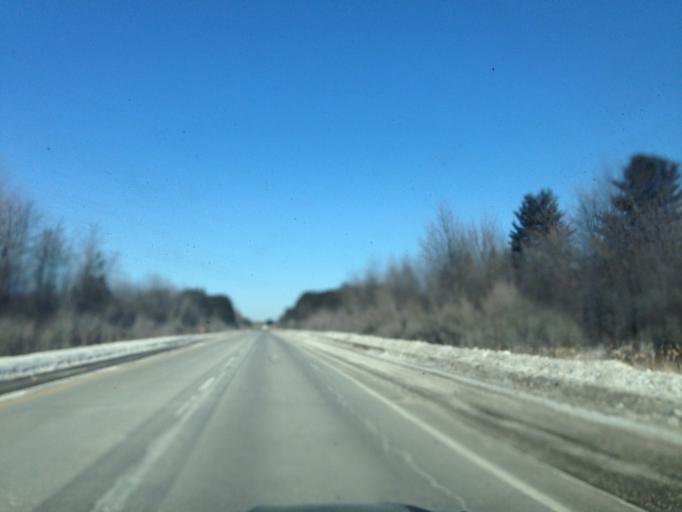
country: CA
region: Ontario
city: Ottawa
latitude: 45.3551
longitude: -75.4665
